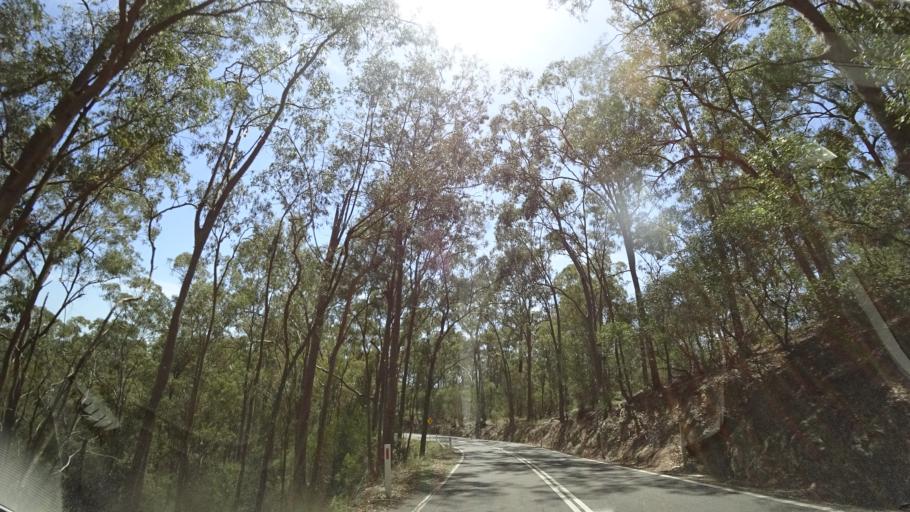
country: AU
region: Queensland
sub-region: Moreton Bay
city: Ferny Hills
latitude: -27.4326
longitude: 152.8927
